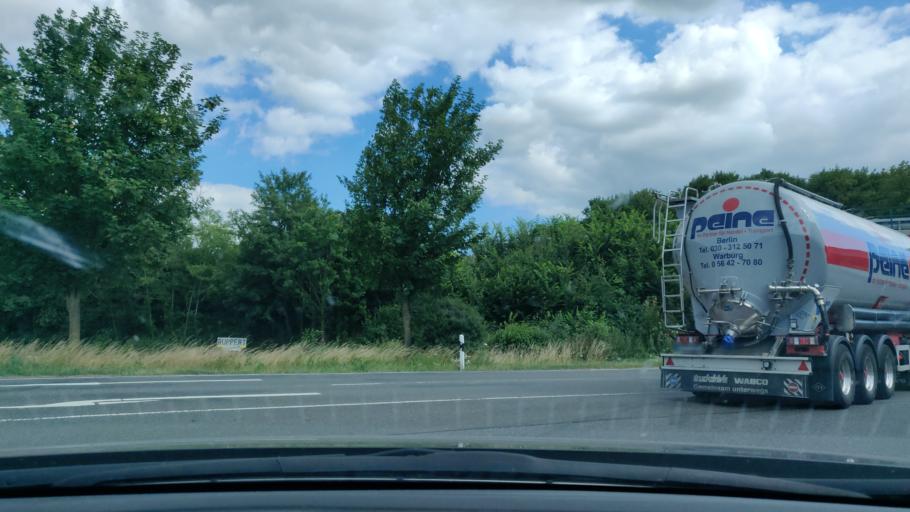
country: DE
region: Hesse
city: Gudensberg
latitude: 51.1851
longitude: 9.3700
